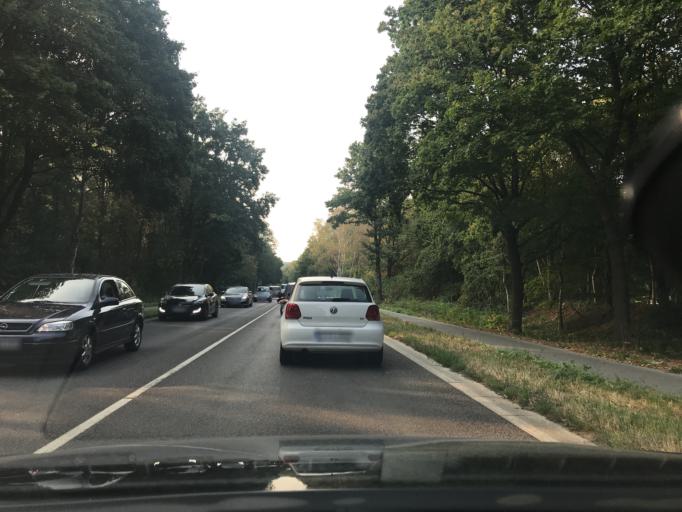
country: DE
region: North Rhine-Westphalia
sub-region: Regierungsbezirk Dusseldorf
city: Erkrath
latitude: 51.2035
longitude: 6.8831
